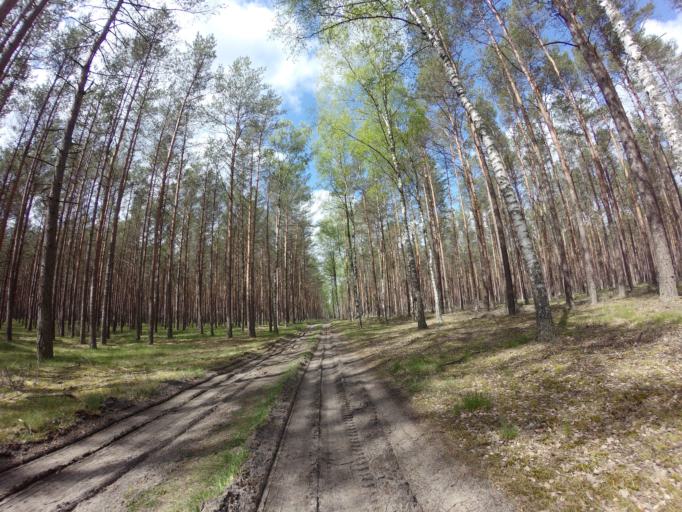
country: PL
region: West Pomeranian Voivodeship
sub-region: Powiat drawski
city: Kalisz Pomorski
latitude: 53.1936
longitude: 15.9889
